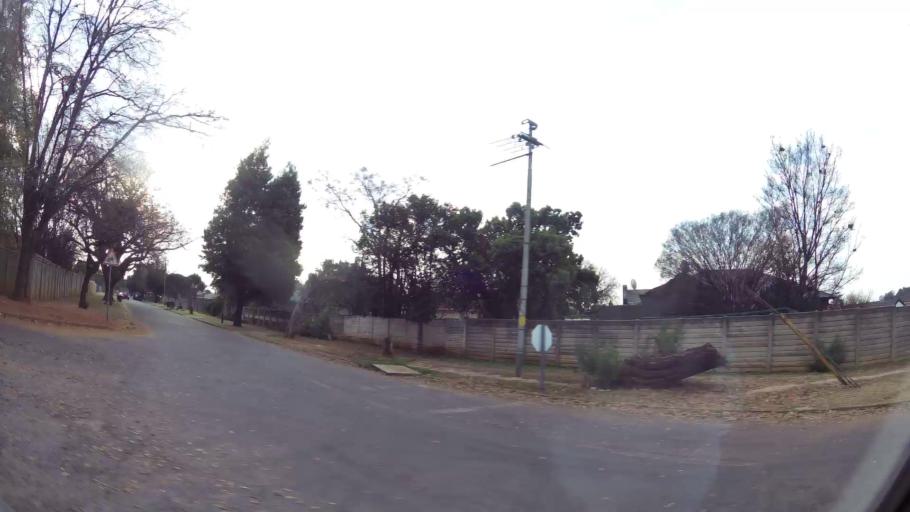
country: ZA
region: Gauteng
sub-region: Ekurhuleni Metropolitan Municipality
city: Germiston
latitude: -26.2330
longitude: 28.1795
